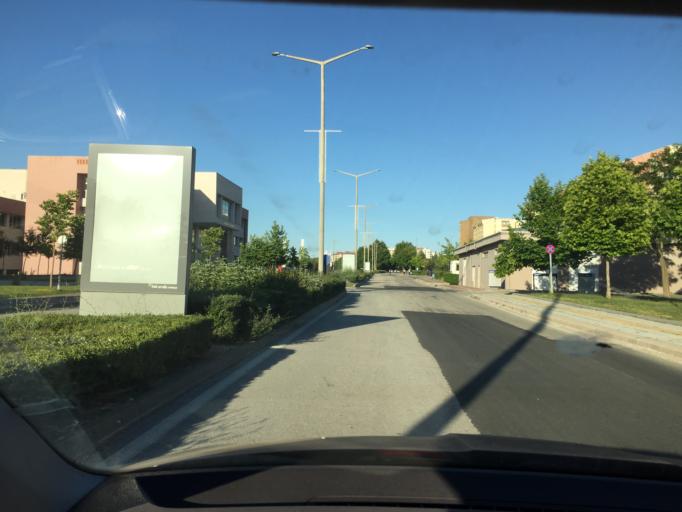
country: TR
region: Eskisehir
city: Eskisehir
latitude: 39.7530
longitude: 30.4854
